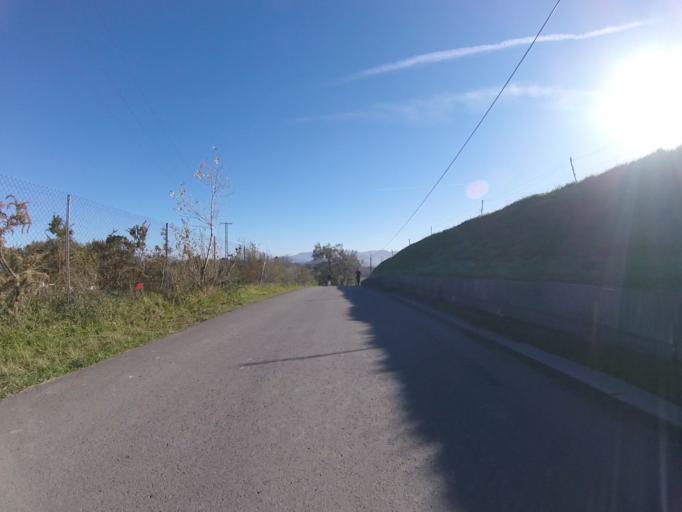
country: ES
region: Basque Country
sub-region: Provincia de Guipuzcoa
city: Lasarte
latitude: 43.2846
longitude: -2.0294
